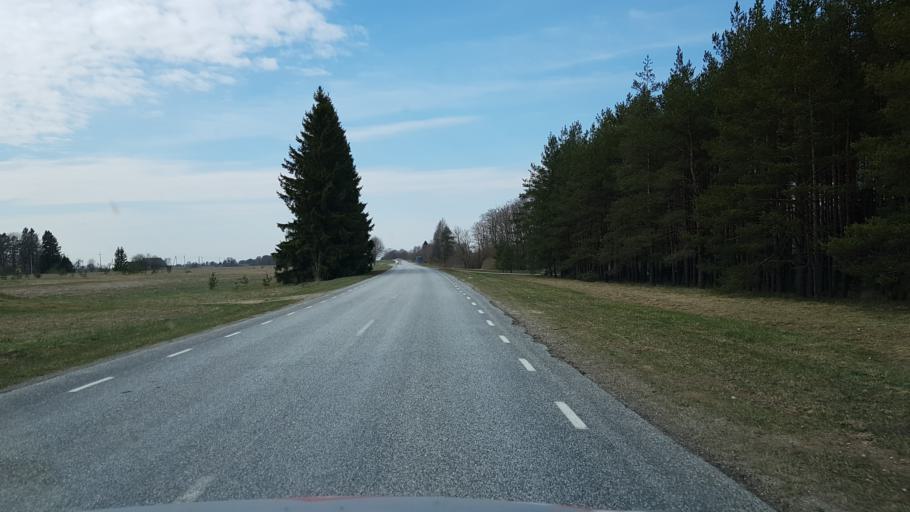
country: EE
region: Laeaene-Virumaa
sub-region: Haljala vald
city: Haljala
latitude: 59.4689
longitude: 26.1782
